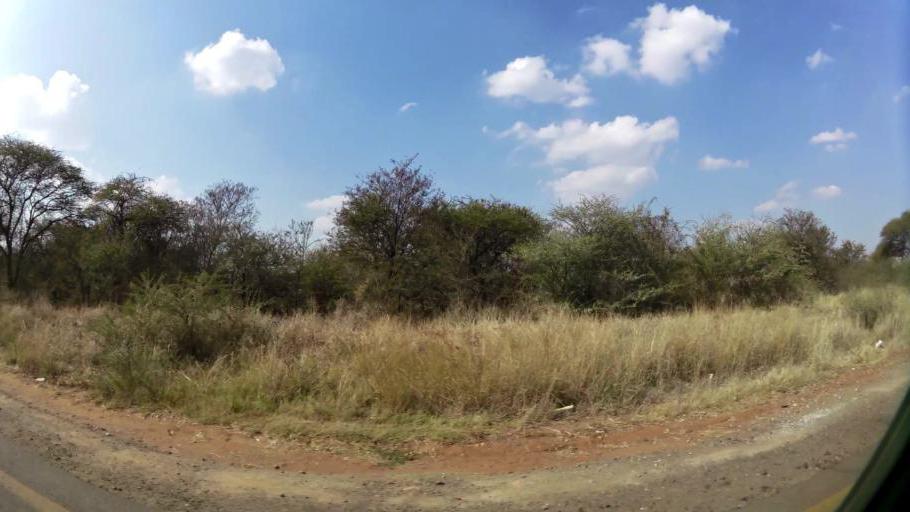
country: ZA
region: North-West
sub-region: Bojanala Platinum District Municipality
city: Mogwase
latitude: -25.4443
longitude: 27.0881
